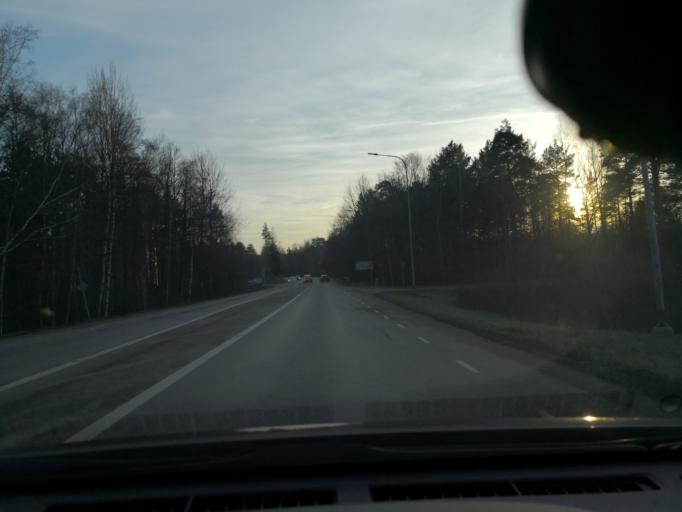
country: SE
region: Vaestmanland
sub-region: Vasteras
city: Vasteras
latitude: 59.6134
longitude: 16.5055
